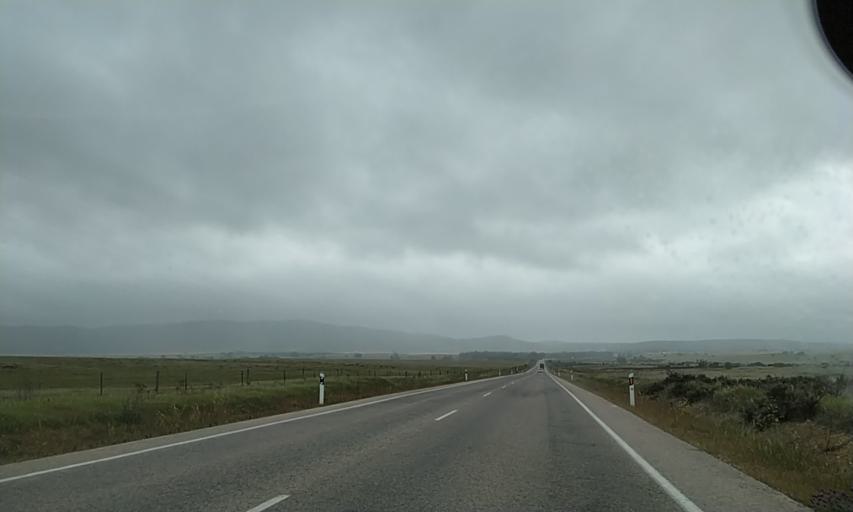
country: ES
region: Extremadura
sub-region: Provincia de Caceres
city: Malpartida de Caceres
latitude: 39.3435
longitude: -6.4750
